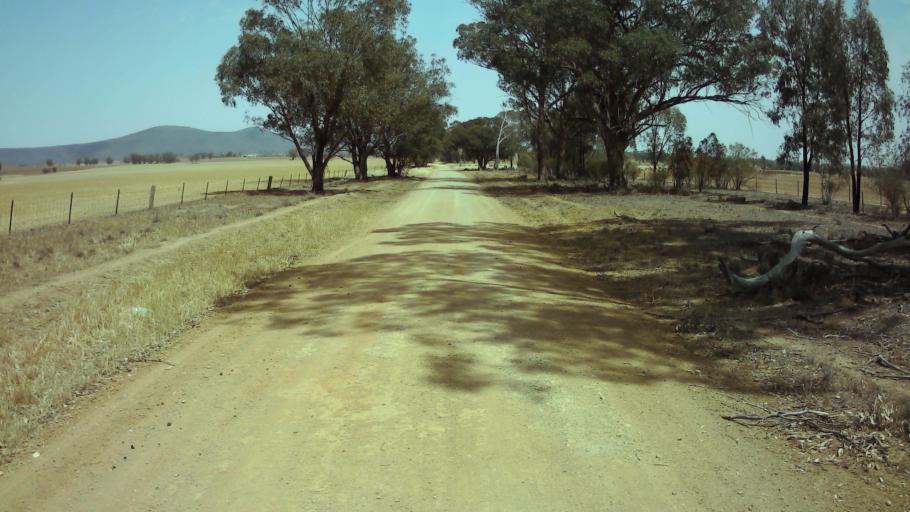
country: AU
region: New South Wales
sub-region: Weddin
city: Grenfell
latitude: -33.8851
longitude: 148.0846
